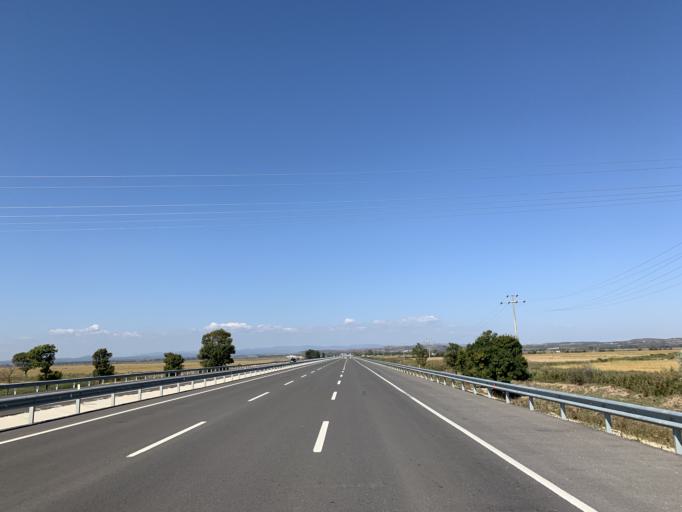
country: TR
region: Edirne
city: Ipsala
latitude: 40.9163
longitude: 26.3580
